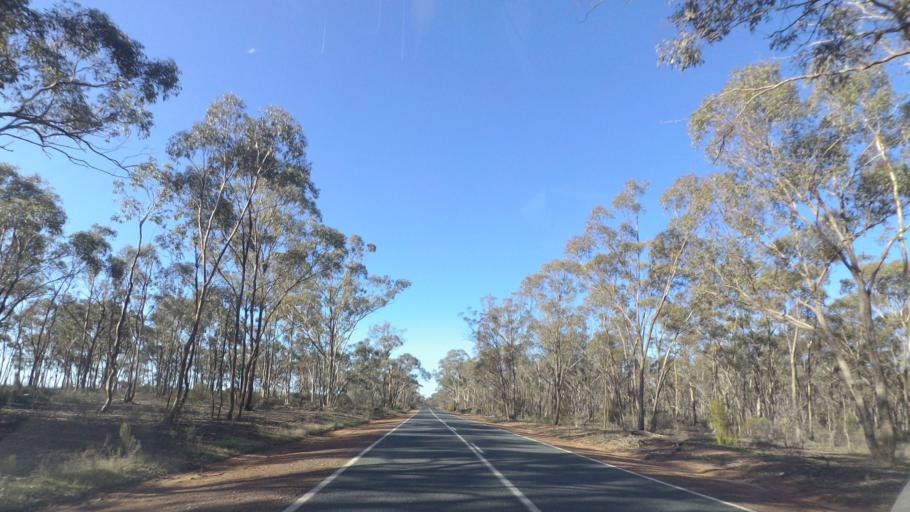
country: AU
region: Victoria
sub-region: Greater Bendigo
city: Epsom
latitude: -36.6711
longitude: 144.4143
